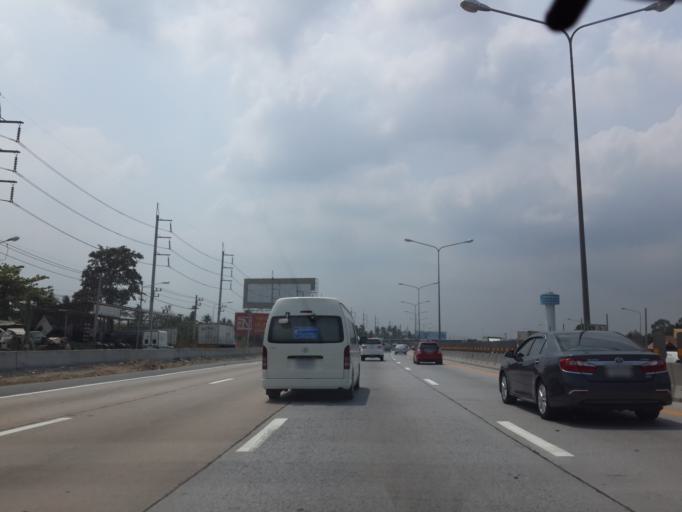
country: TH
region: Chon Buri
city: Si Racha
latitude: 13.2134
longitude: 101.0056
